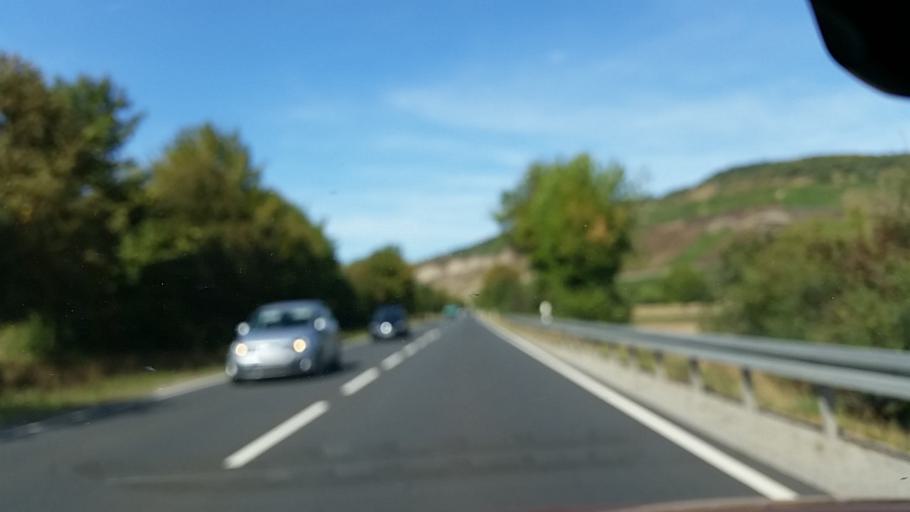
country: DE
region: Bavaria
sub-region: Regierungsbezirk Unterfranken
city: Thungersheim
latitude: 49.8855
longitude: 9.8377
